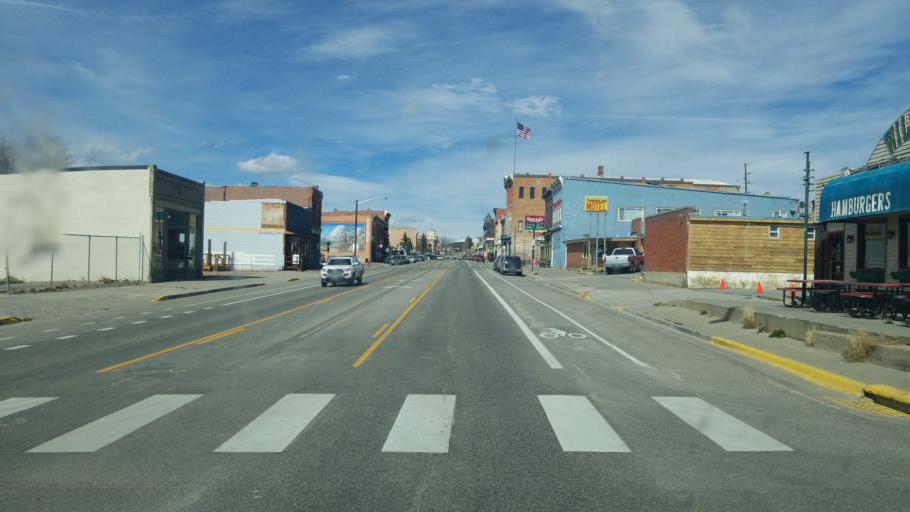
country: US
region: Colorado
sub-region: Lake County
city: Leadville
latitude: 39.2453
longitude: -106.2906
